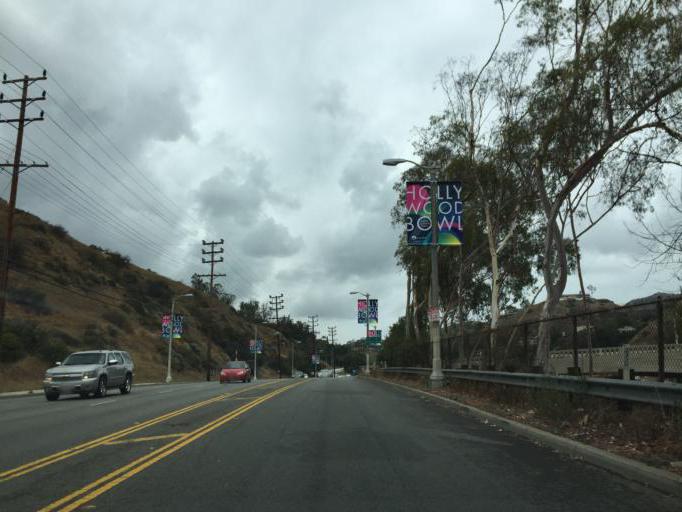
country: US
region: California
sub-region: Los Angeles County
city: Hollywood
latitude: 34.1137
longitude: -118.3367
